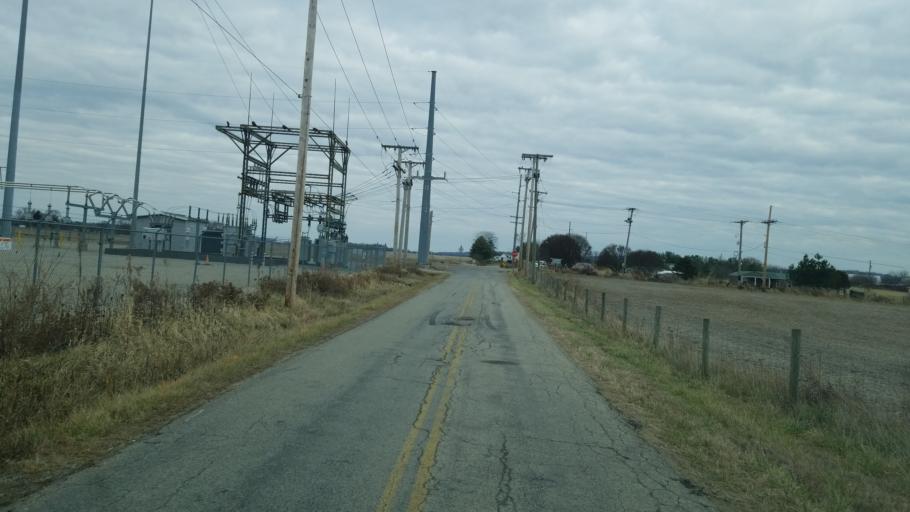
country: US
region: Ohio
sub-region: Highland County
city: Greenfield
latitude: 39.3252
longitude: -83.3534
